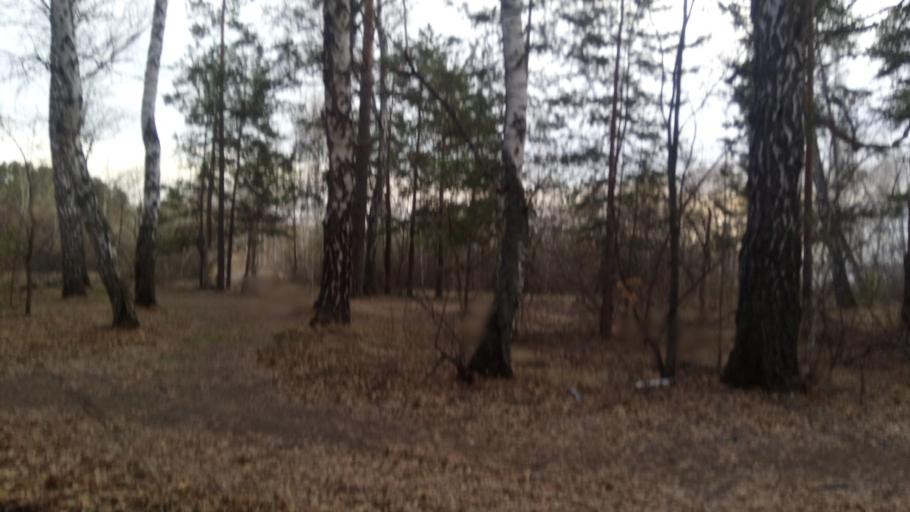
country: RU
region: Chelyabinsk
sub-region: Gorod Chelyabinsk
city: Chelyabinsk
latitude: 55.1419
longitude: 61.3320
